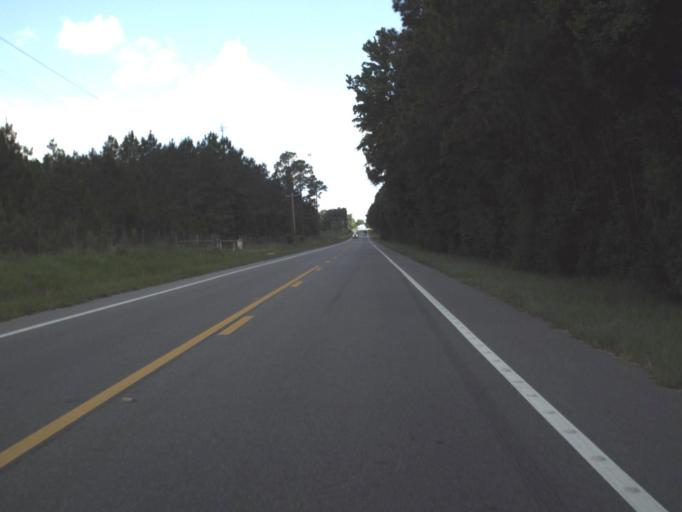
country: US
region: Florida
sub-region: Putnam County
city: Interlachen
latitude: 29.7172
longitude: -81.8071
